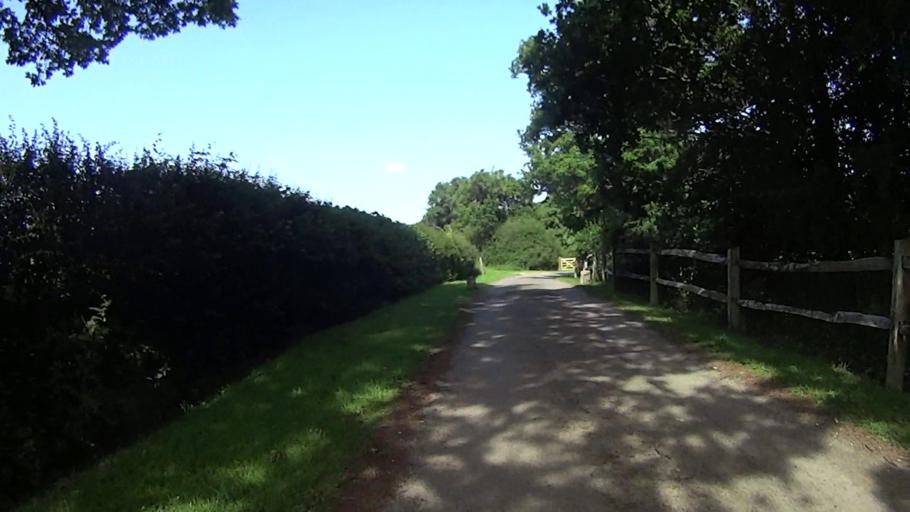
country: GB
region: England
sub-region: West Sussex
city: Bewbush
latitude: 51.1129
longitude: -0.2692
